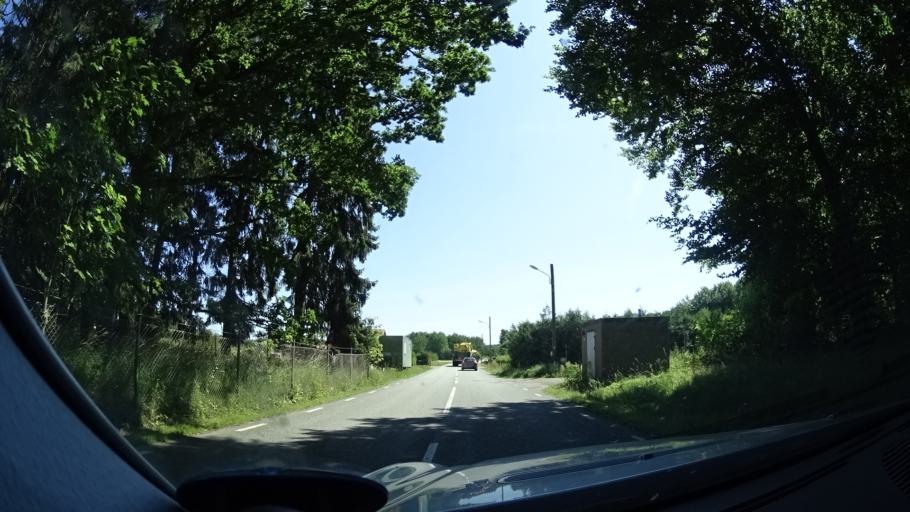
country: SE
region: Skane
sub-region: Kristianstads Kommun
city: Degeberga
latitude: 55.9157
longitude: 13.9843
